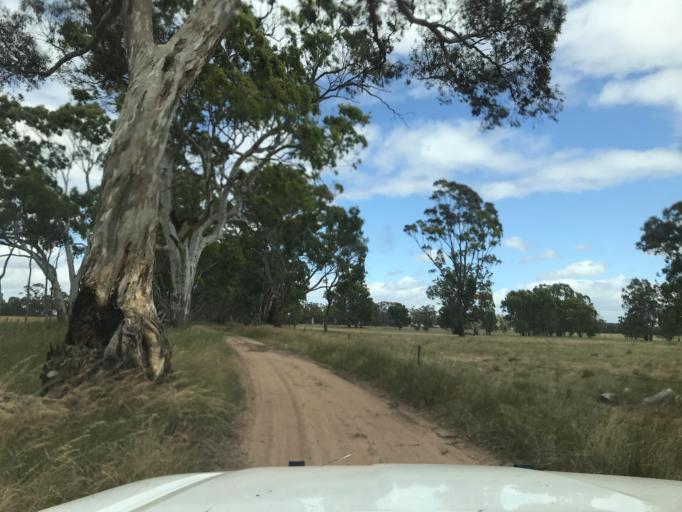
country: AU
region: South Australia
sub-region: Naracoorte and Lucindale
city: Naracoorte
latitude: -36.8998
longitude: 141.3953
